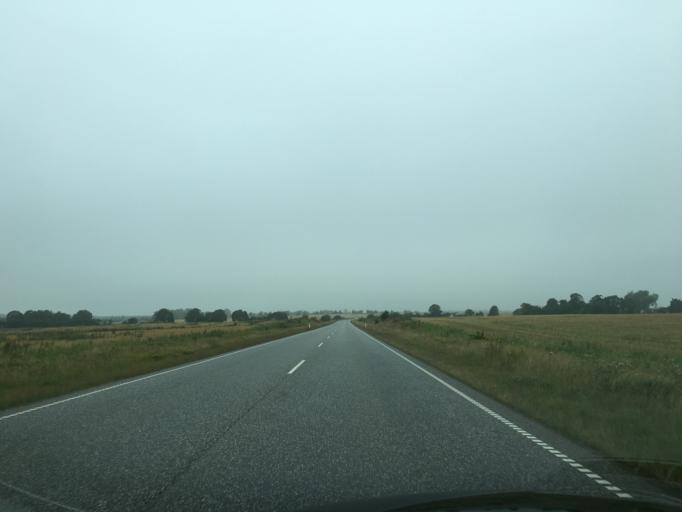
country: DK
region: South Denmark
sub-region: Kolding Kommune
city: Kolding
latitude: 55.5471
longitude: 9.4603
